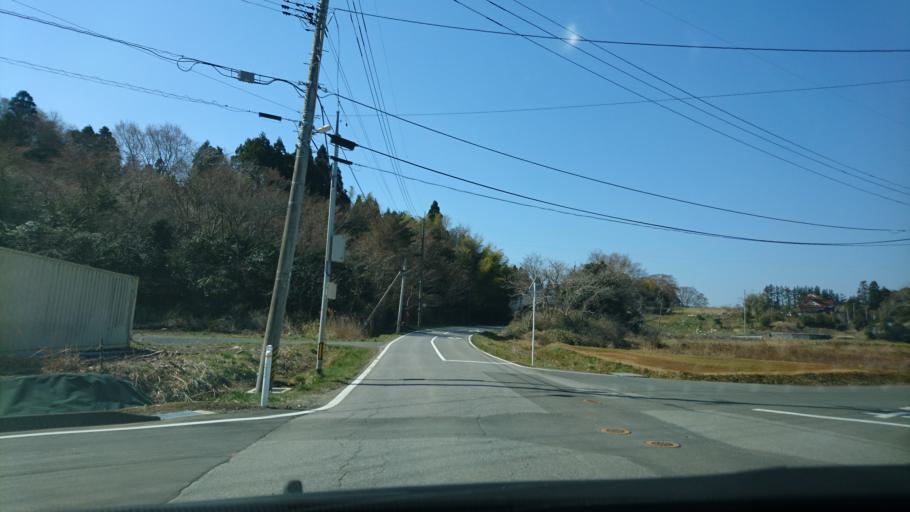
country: JP
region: Iwate
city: Ofunato
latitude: 38.8624
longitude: 141.6096
